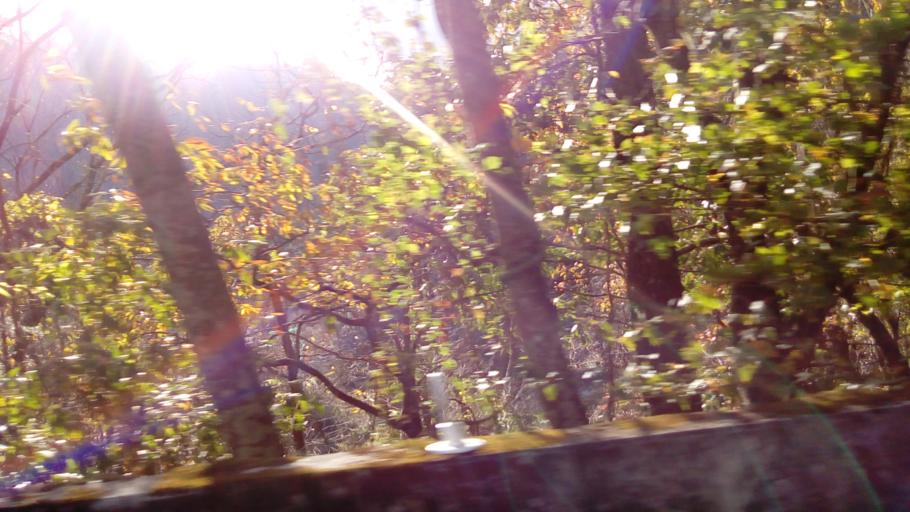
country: TW
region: Taiwan
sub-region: Hualien
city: Hualian
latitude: 24.3461
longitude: 121.3158
